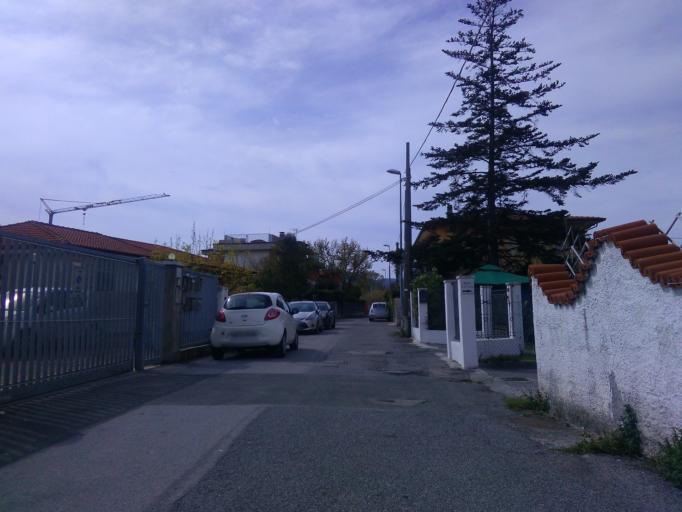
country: IT
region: Tuscany
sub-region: Provincia di Massa-Carrara
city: Marina di Carrara
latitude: 44.0487
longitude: 10.0259
